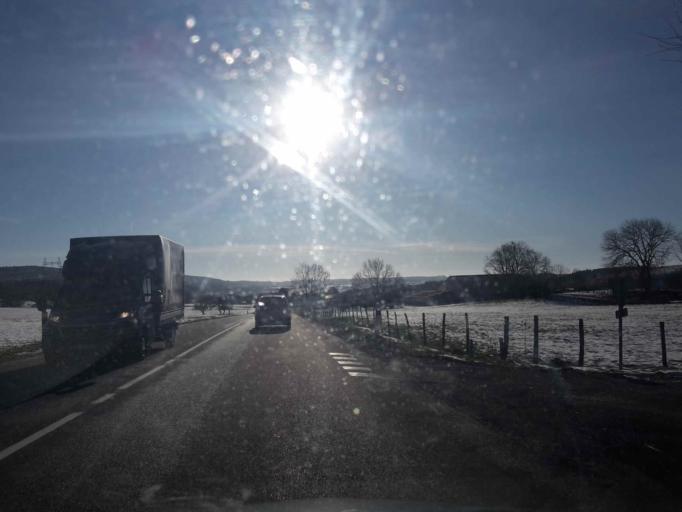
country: FR
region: Franche-Comte
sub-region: Departement du Doubs
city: Doubs
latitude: 47.0238
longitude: 6.3291
